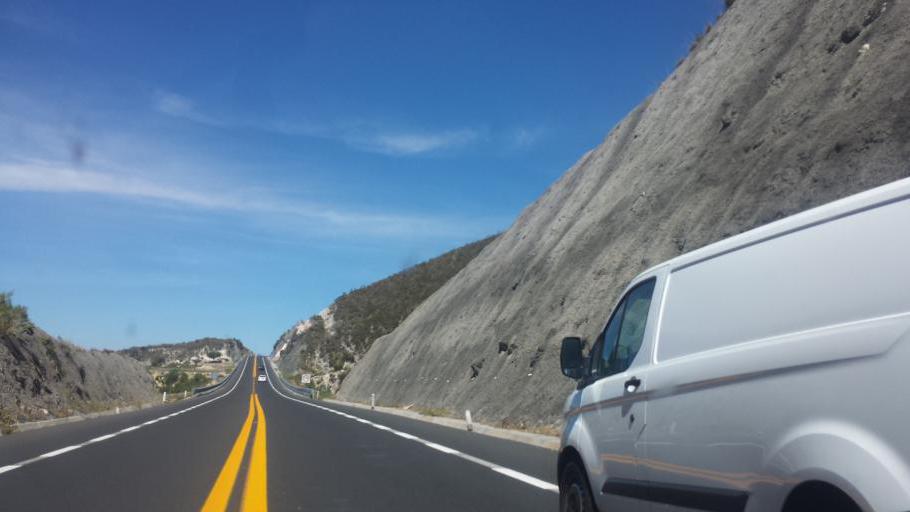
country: MX
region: Puebla
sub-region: San Jose Miahuatlan
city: San Pedro Tetitlan
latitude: 18.0022
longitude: -97.3552
